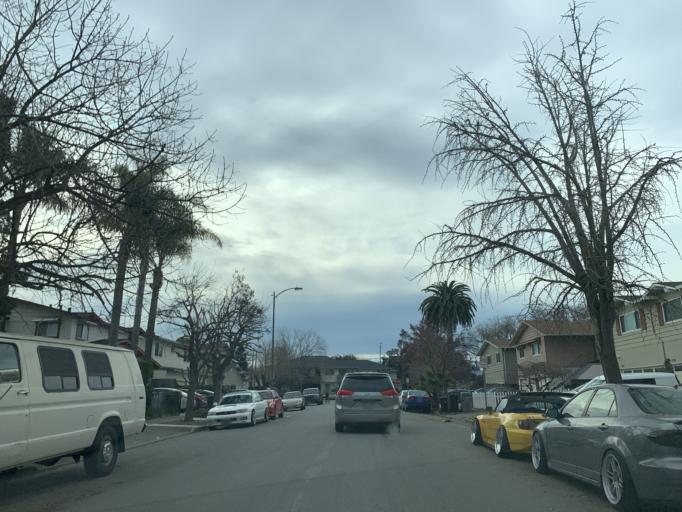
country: US
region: California
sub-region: Santa Clara County
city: Buena Vista
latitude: 37.3141
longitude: -121.9174
